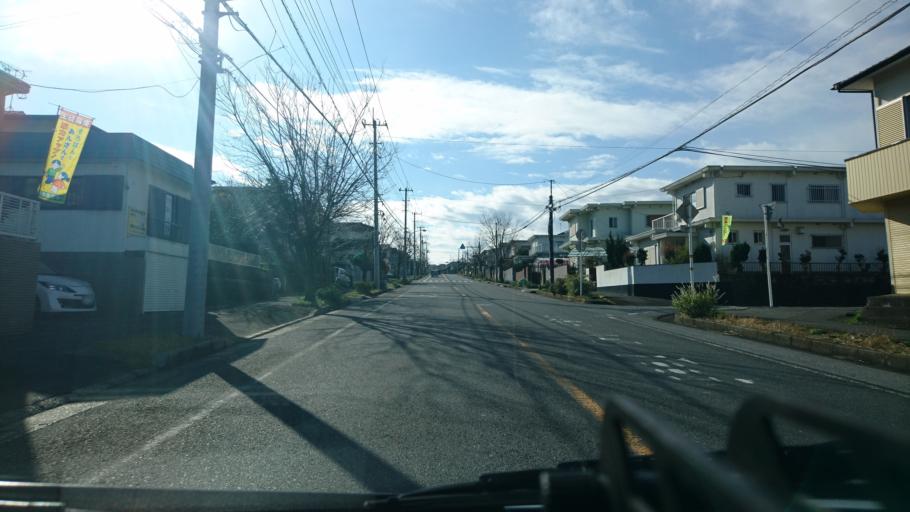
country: JP
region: Chiba
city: Kisarazu
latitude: 35.3595
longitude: 139.9345
